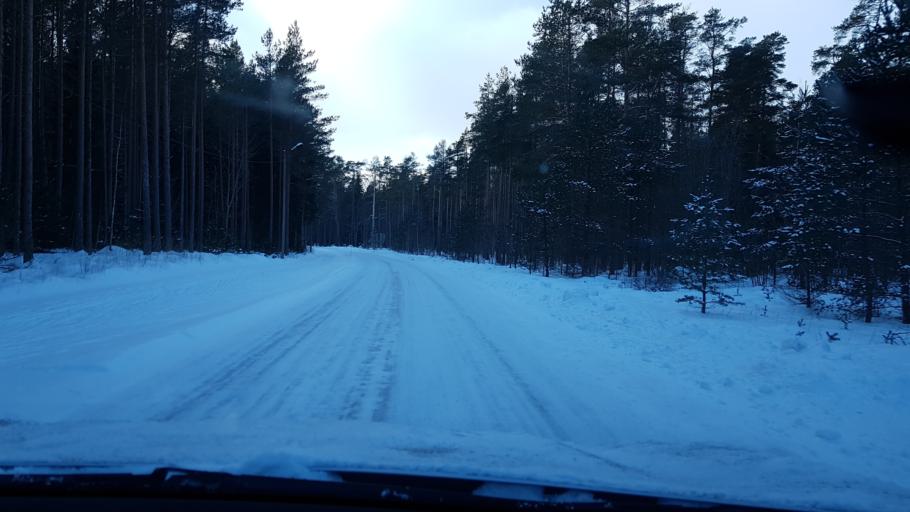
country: EE
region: Harju
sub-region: Nissi vald
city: Turba
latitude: 59.2239
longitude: 24.1520
